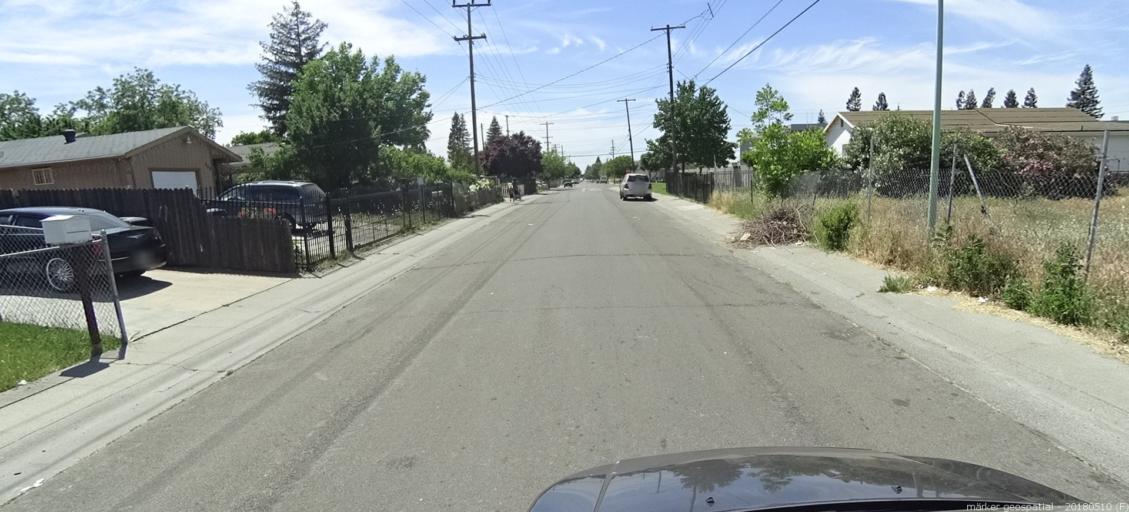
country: US
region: California
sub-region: Sacramento County
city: Rio Linda
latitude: 38.6385
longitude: -121.4513
